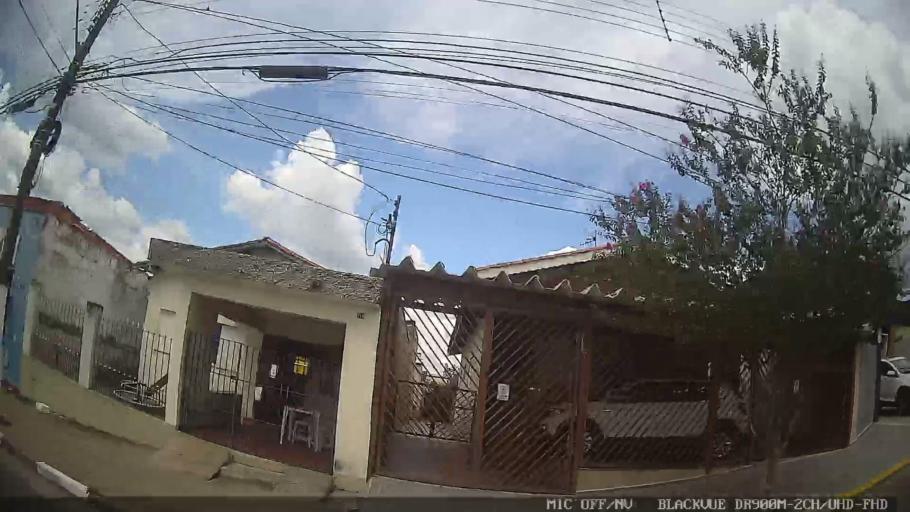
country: BR
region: Sao Paulo
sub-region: Atibaia
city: Atibaia
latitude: -23.1186
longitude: -46.5686
